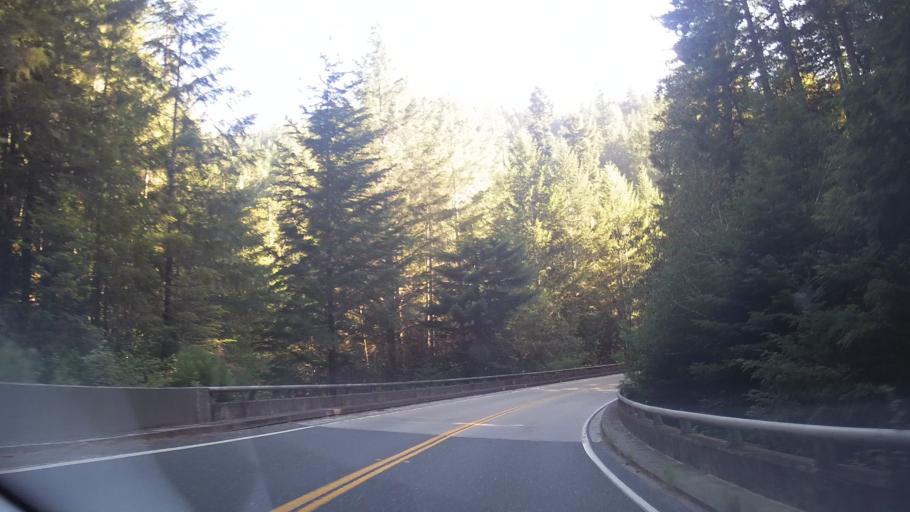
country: US
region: California
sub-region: Mendocino County
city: Brooktrails
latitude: 39.3489
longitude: -123.5116
